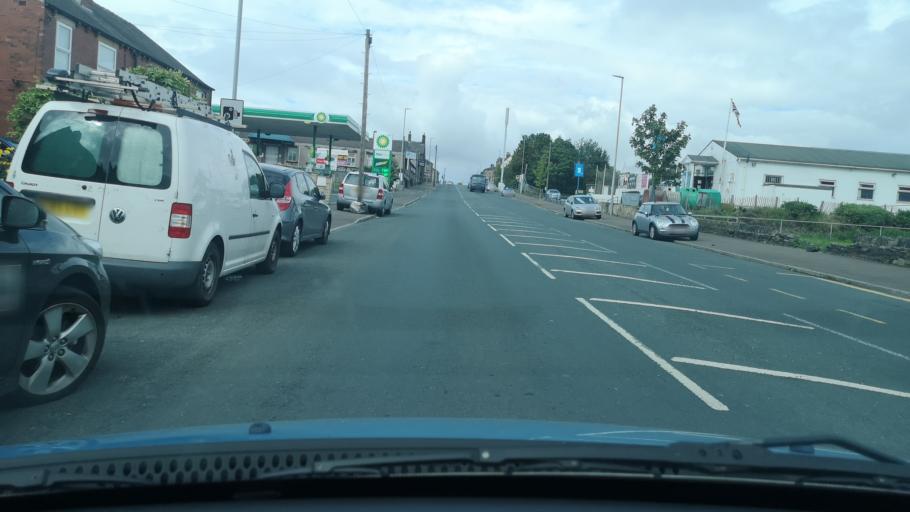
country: GB
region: England
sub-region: Kirklees
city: Batley
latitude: 53.7054
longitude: -1.6508
